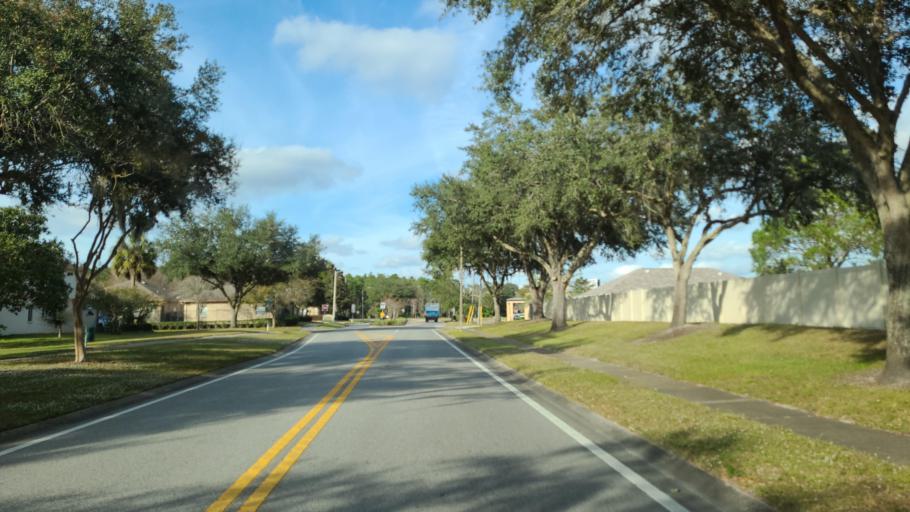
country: US
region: Florida
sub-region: Pasco County
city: Land O' Lakes
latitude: 28.1840
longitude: -82.4077
